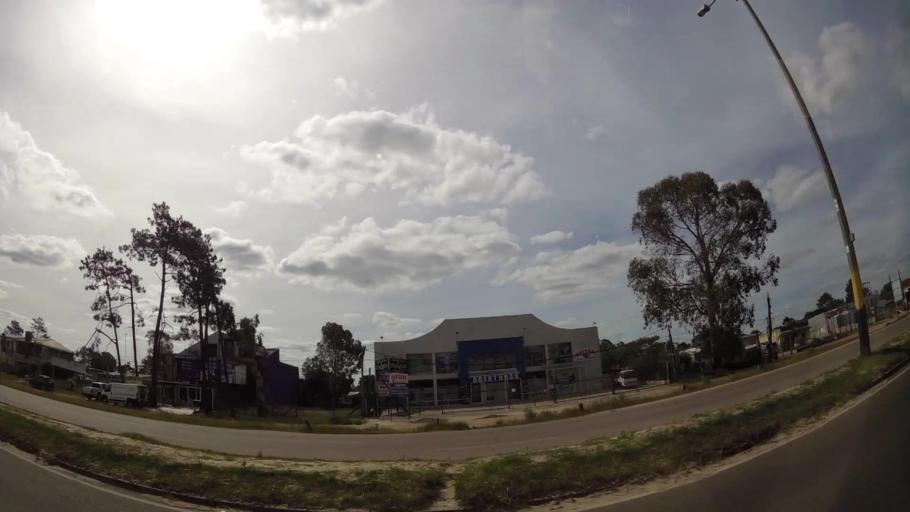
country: UY
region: Canelones
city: Colonia Nicolich
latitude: -34.8165
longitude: -55.9484
